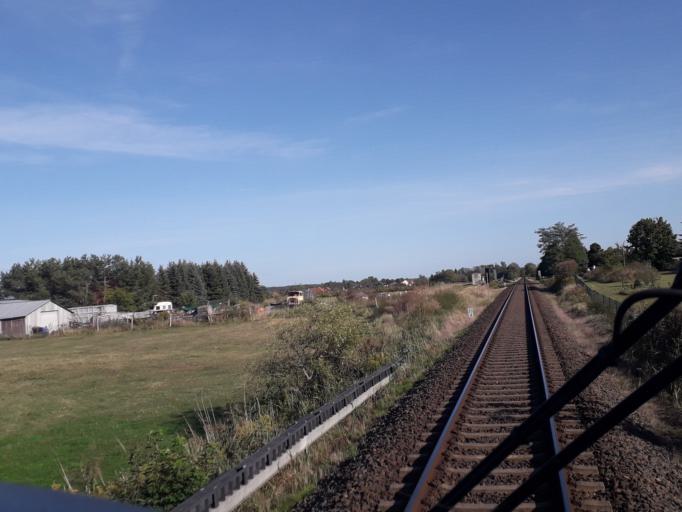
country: DE
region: Brandenburg
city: Kremmen
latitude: 52.7443
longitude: 13.0603
